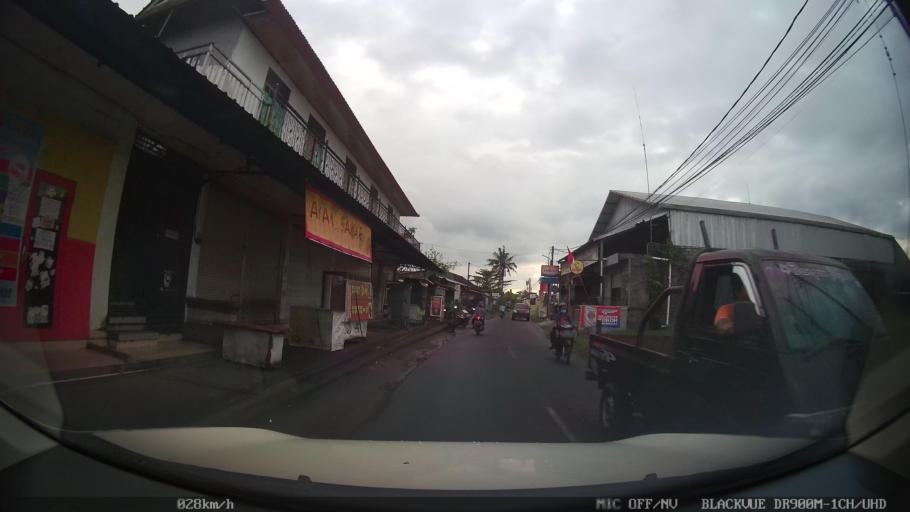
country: ID
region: Bali
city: Banjar Paangkelod
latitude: -8.6189
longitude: 115.2582
